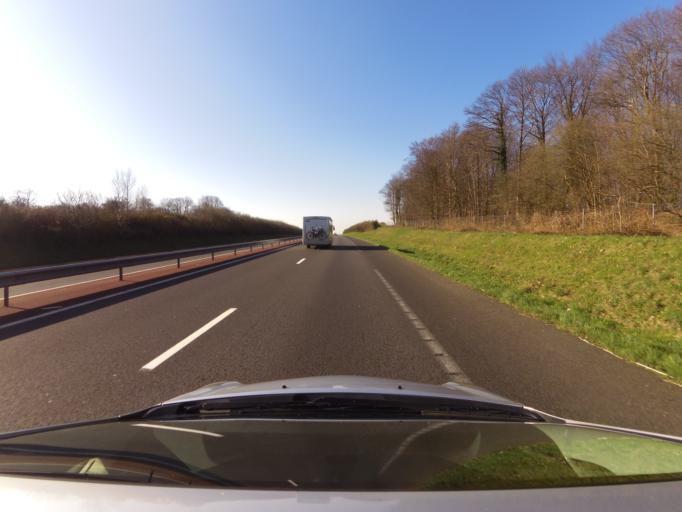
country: FR
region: Lower Normandy
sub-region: Departement de la Manche
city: Villedieu-les-Poeles
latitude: 48.7671
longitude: -1.2777
